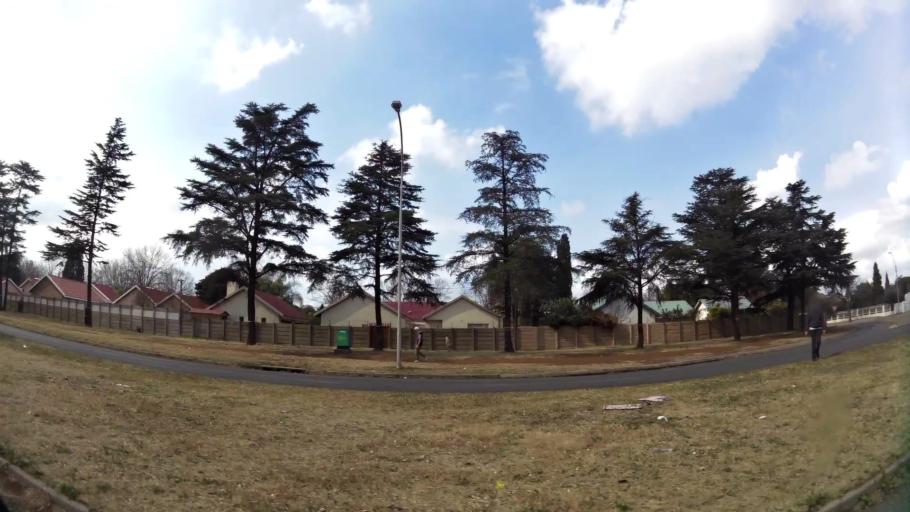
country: ZA
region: Gauteng
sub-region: Sedibeng District Municipality
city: Vanderbijlpark
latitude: -26.7118
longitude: 27.8361
